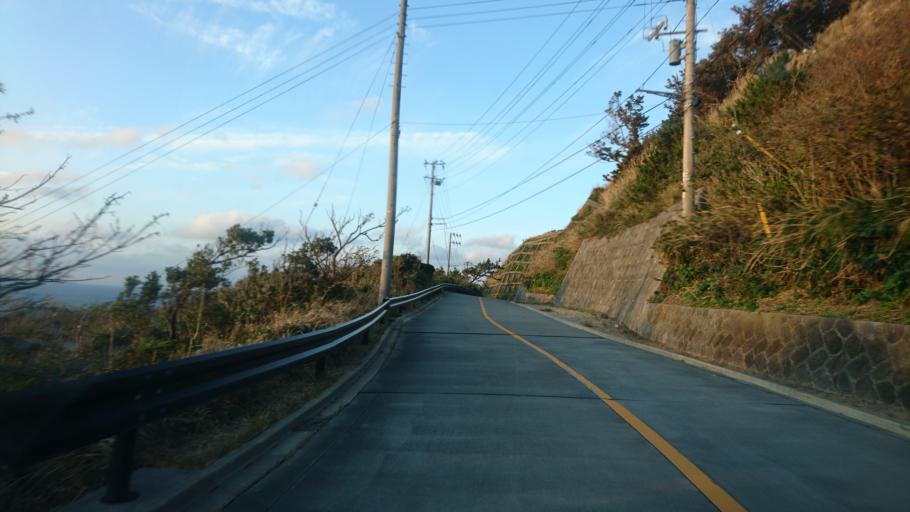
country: JP
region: Shizuoka
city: Shimoda
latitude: 34.3641
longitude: 139.2440
